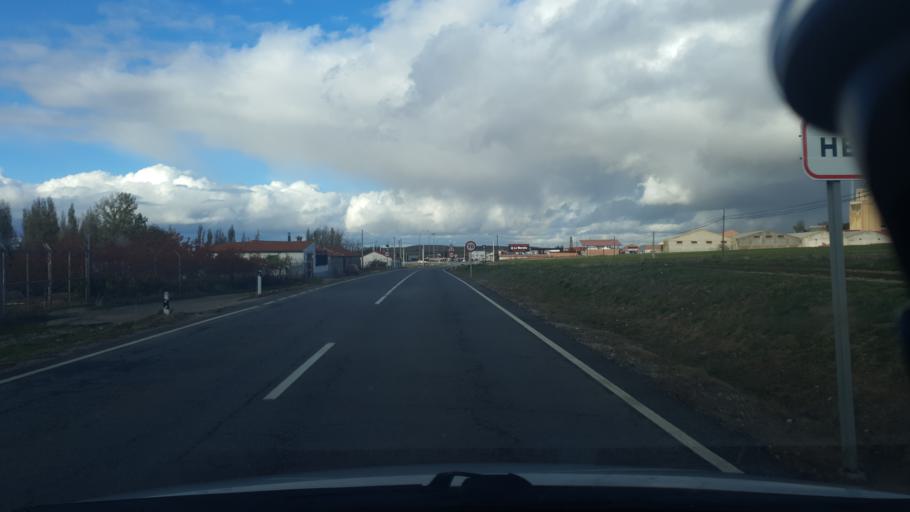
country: ES
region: Castille and Leon
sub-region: Provincia de Avila
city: Hernansancho
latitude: 40.8521
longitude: -4.7305
